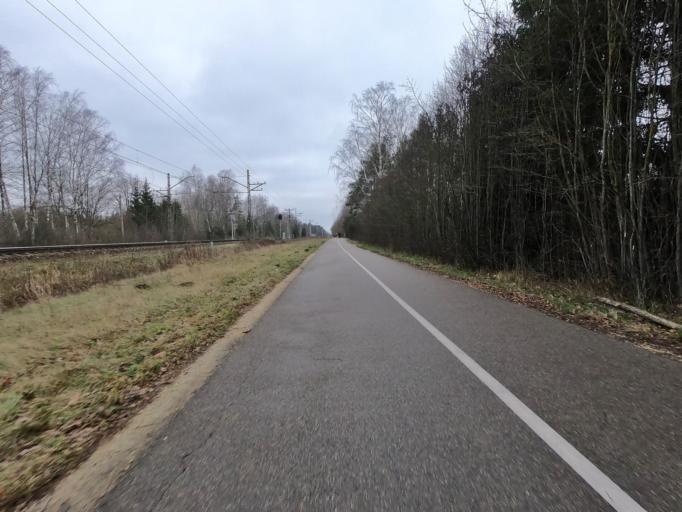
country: LV
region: Babite
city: Pinki
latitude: 56.9517
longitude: 23.9804
